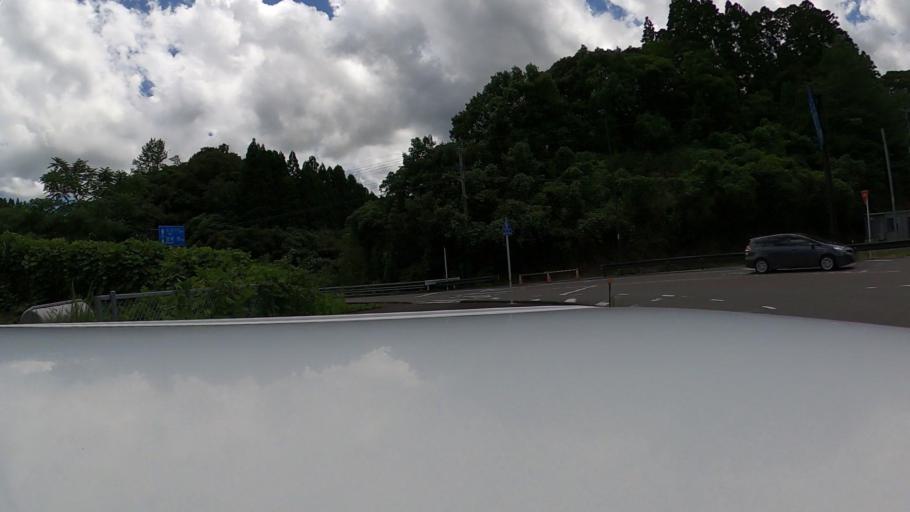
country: JP
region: Miyazaki
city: Nobeoka
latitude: 32.5946
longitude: 131.4972
